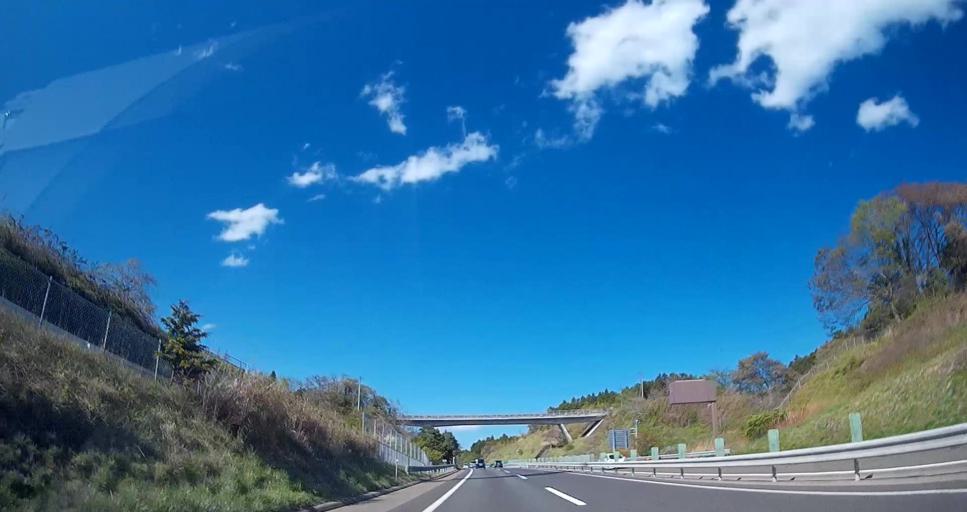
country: JP
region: Miyagi
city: Rifu
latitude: 38.3266
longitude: 140.9936
